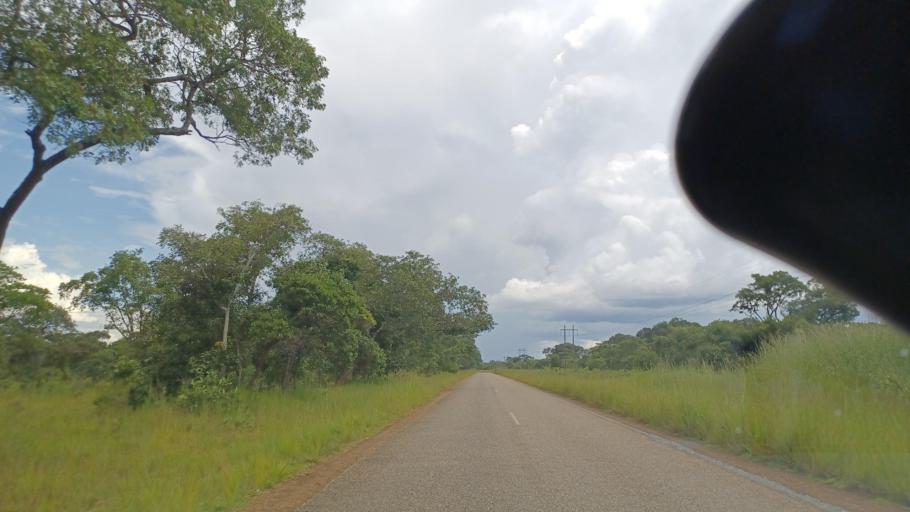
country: ZM
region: North-Western
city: Kasempa
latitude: -13.1477
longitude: 25.8776
